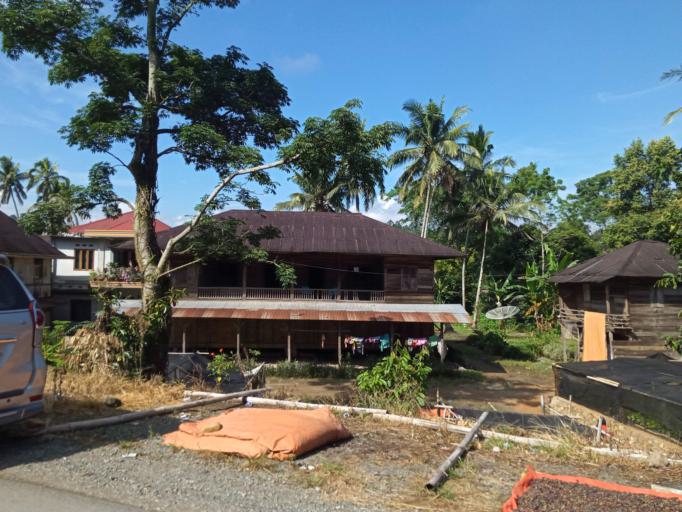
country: ID
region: Jambi
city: Sungai Penuh
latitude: -2.1652
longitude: 101.5924
